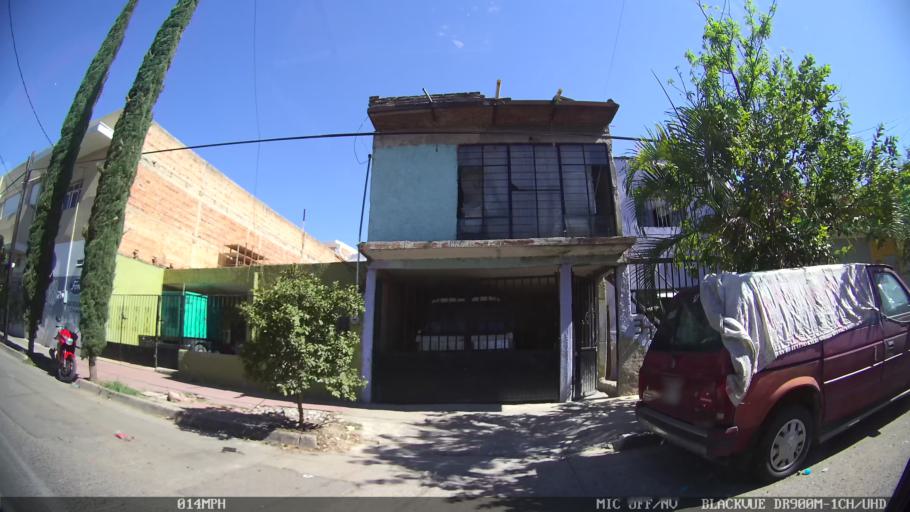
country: MX
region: Jalisco
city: Tlaquepaque
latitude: 20.6537
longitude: -103.2843
